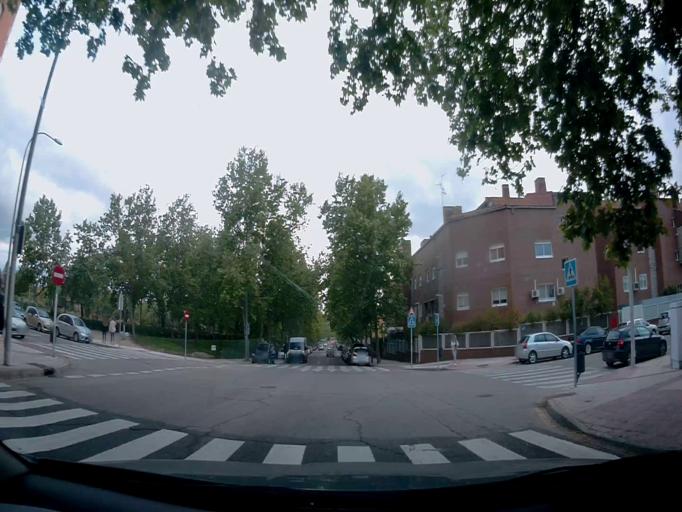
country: ES
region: Madrid
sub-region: Provincia de Madrid
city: Alcorcon
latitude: 40.3371
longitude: -3.8338
